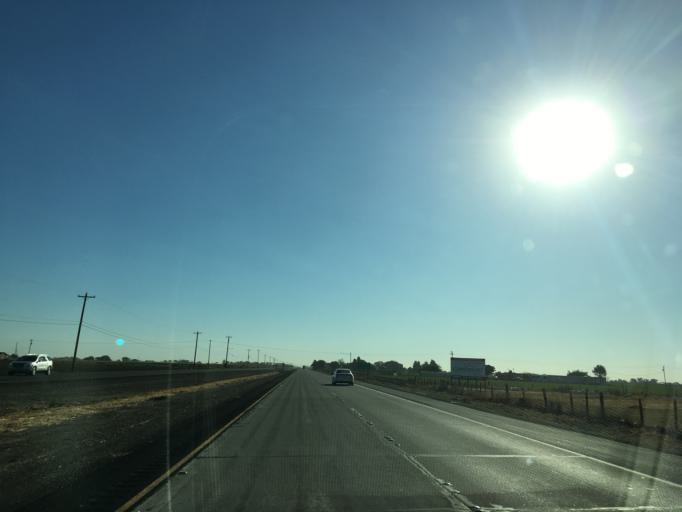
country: US
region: California
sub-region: Merced County
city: Los Banos
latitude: 37.0566
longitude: -120.9166
